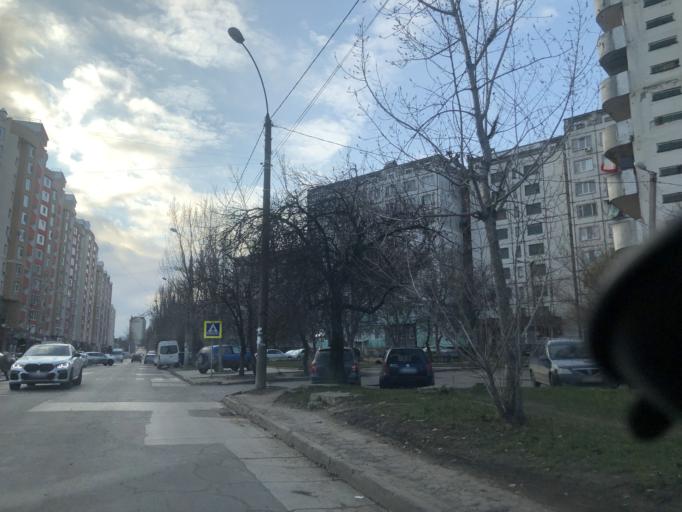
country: MD
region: Chisinau
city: Chisinau
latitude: 47.0358
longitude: 28.8874
